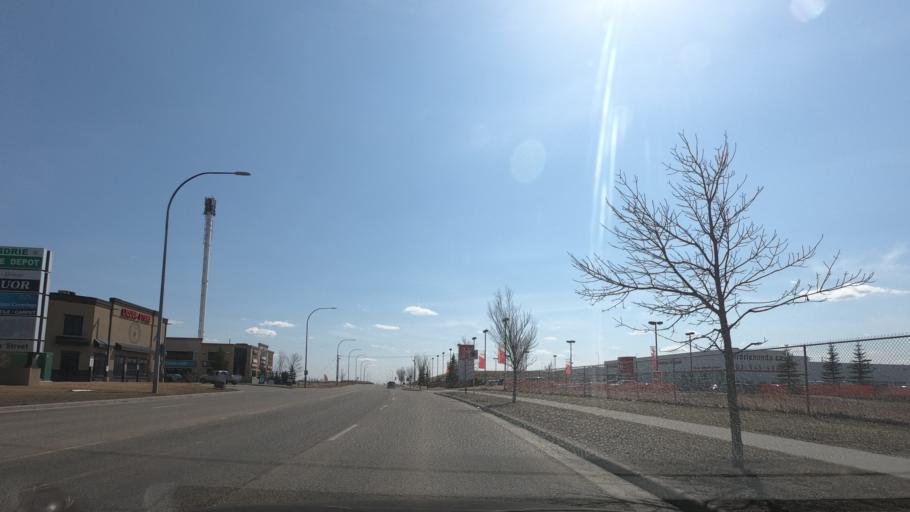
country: CA
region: Alberta
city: Airdrie
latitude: 51.2592
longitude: -114.0050
